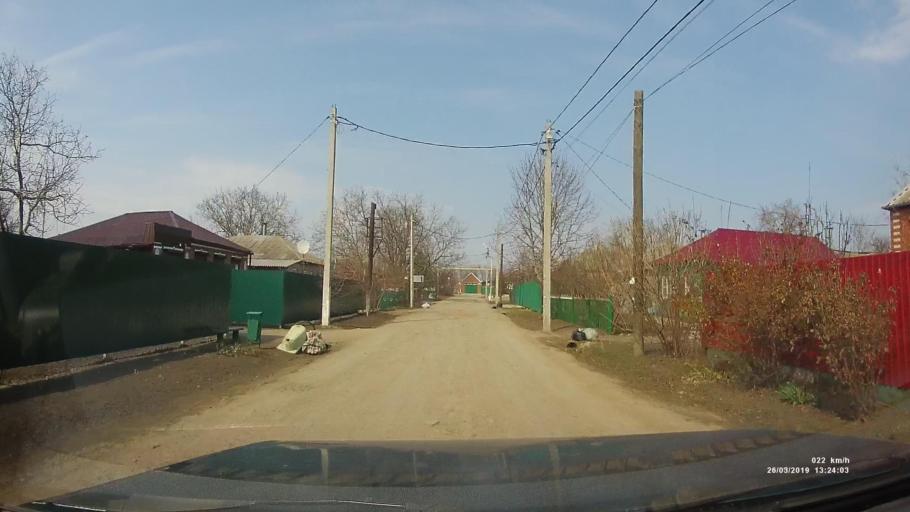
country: RU
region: Rostov
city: Novobessergenovka
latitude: 47.1739
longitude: 38.7661
